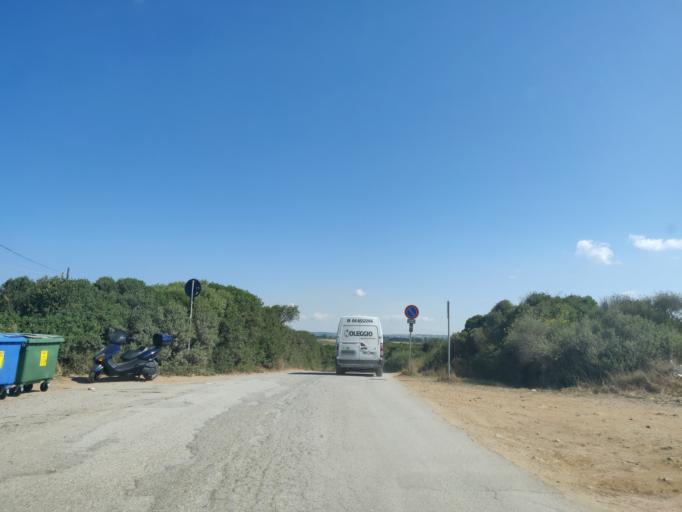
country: IT
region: Latium
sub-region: Citta metropolitana di Roma Capitale
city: Aurelia
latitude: 42.1700
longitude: 11.7411
